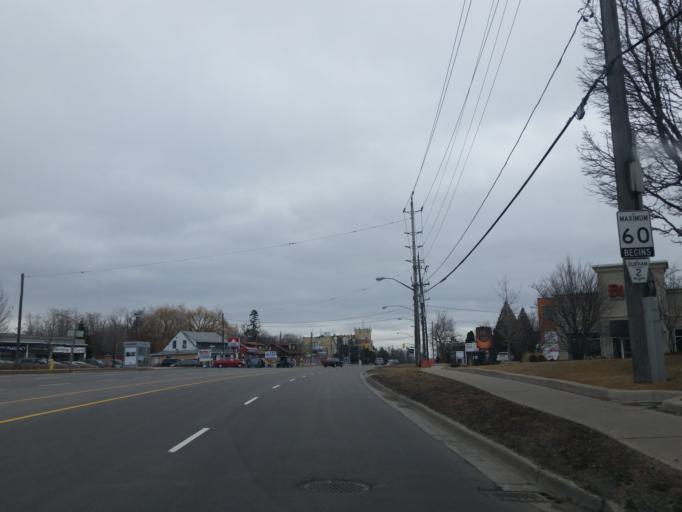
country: CA
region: Ontario
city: Pickering
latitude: 43.8081
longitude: -79.1317
